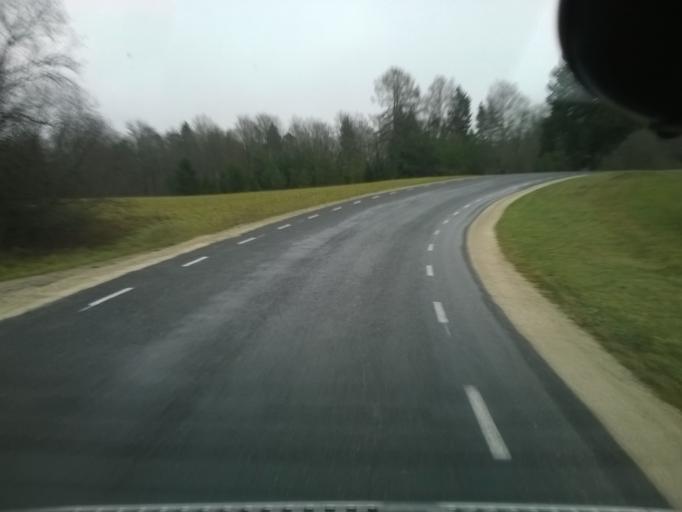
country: EE
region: Harju
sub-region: Saue linn
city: Saue
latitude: 59.1400
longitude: 24.5065
